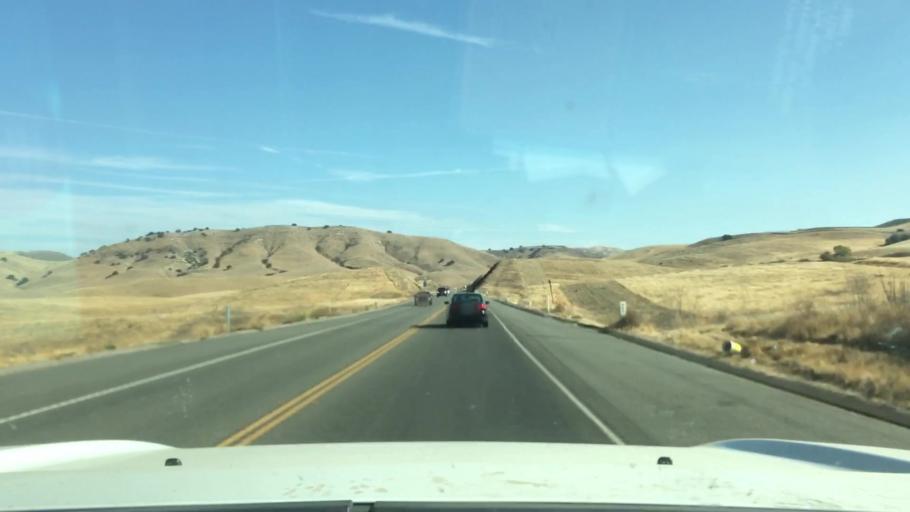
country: US
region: California
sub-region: San Luis Obispo County
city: Shandon
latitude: 35.7426
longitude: -120.2412
